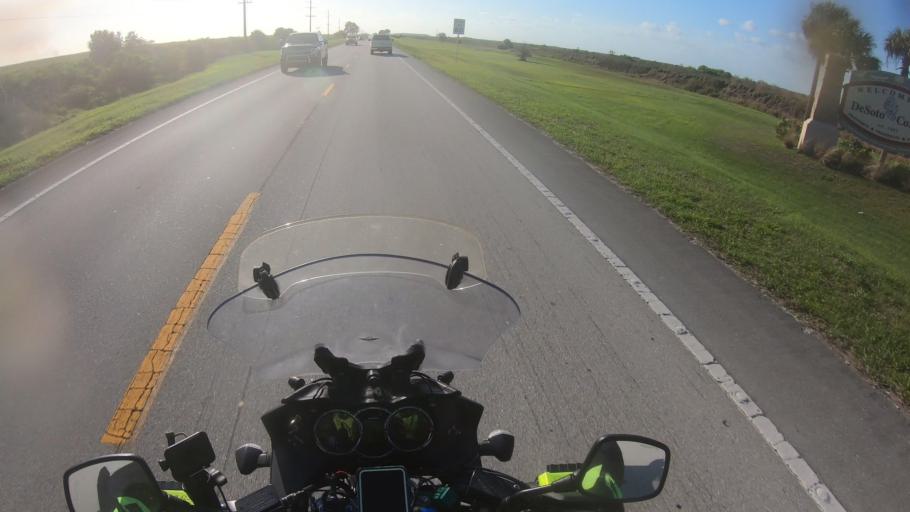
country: US
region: Florida
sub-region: Highlands County
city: Placid Lakes
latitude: 27.2098
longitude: -81.5663
